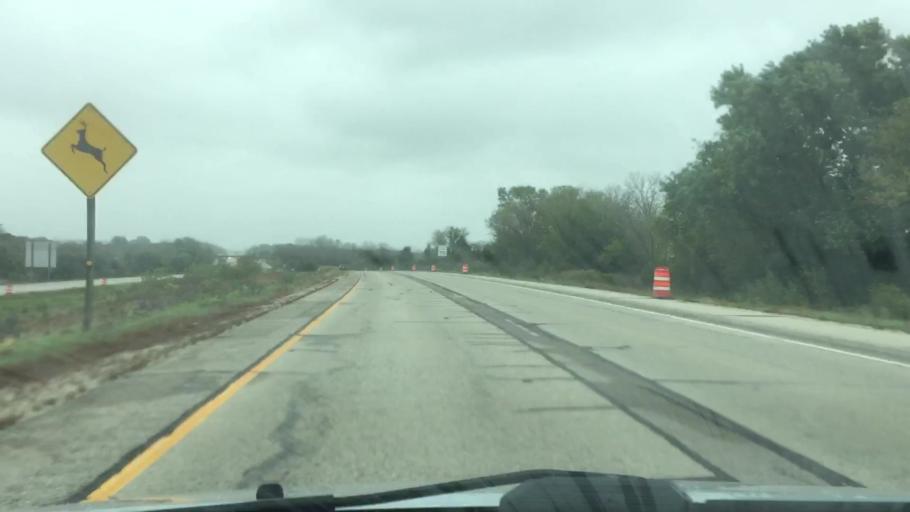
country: US
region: Wisconsin
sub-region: Walworth County
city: Lake Geneva
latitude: 42.5866
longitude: -88.4020
